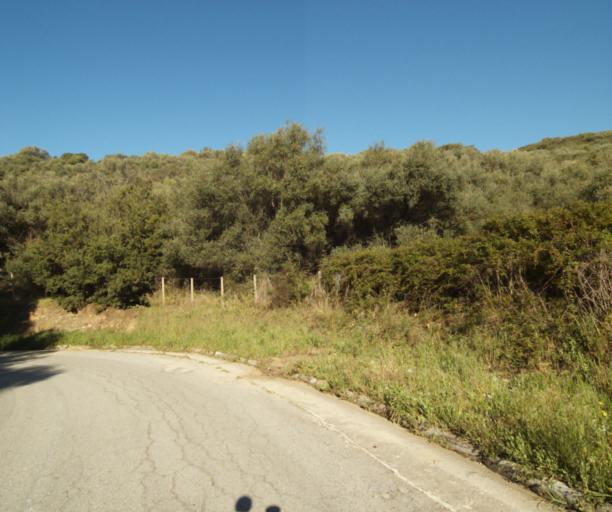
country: FR
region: Corsica
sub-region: Departement de la Corse-du-Sud
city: Propriano
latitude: 41.6664
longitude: 8.8939
